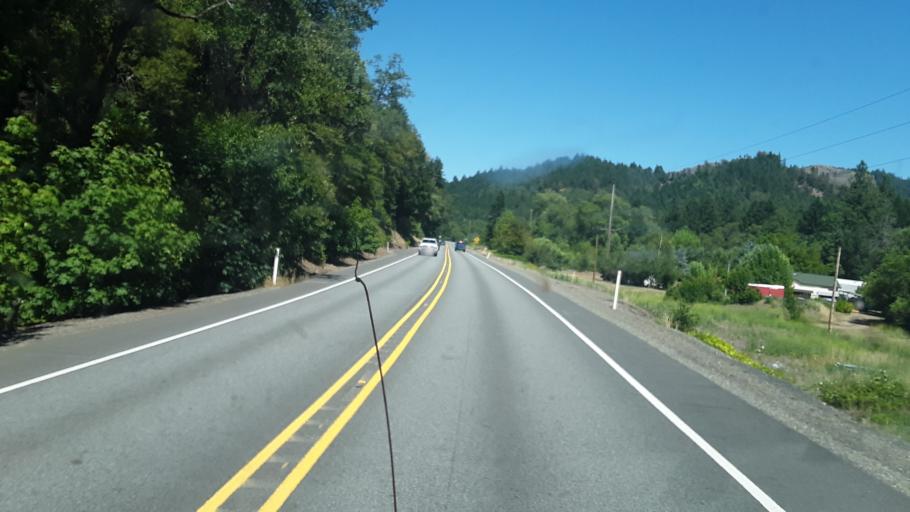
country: US
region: Oregon
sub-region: Josephine County
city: Redwood
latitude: 42.3627
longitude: -123.5167
